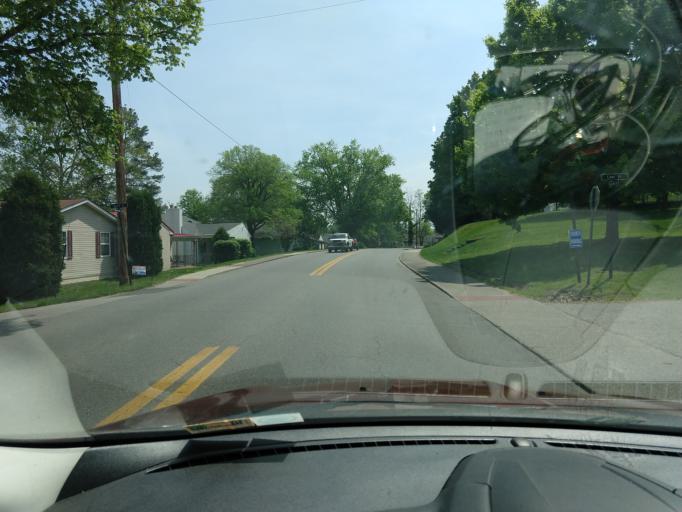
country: US
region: West Virginia
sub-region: Kanawha County
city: Saint Albans
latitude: 38.3825
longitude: -81.8287
